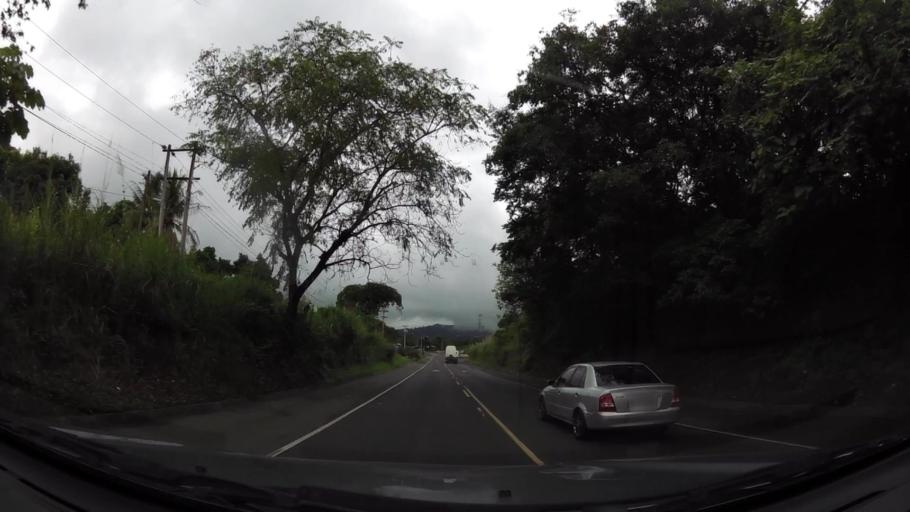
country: PA
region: Colon
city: Nuevo Vigia
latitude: 9.2000
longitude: -79.6247
